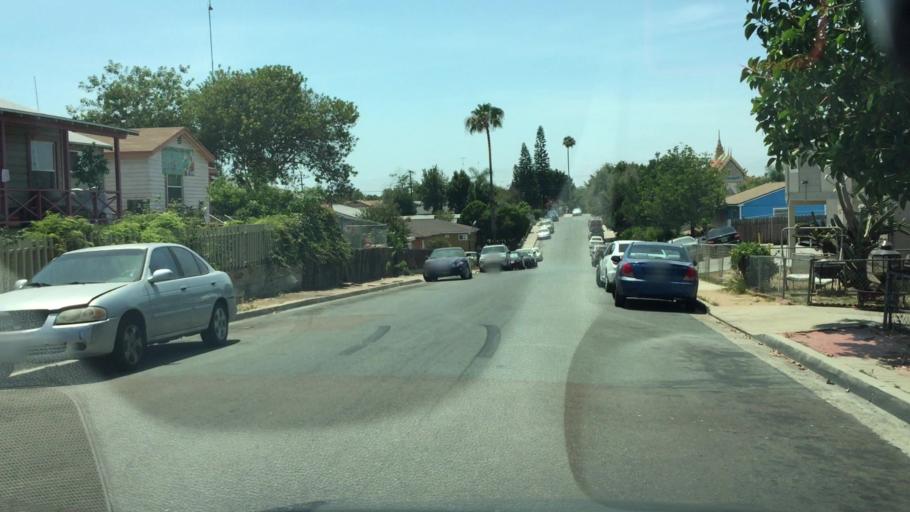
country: US
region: California
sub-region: San Diego County
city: Lemon Grove
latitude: 32.7482
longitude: -117.0817
